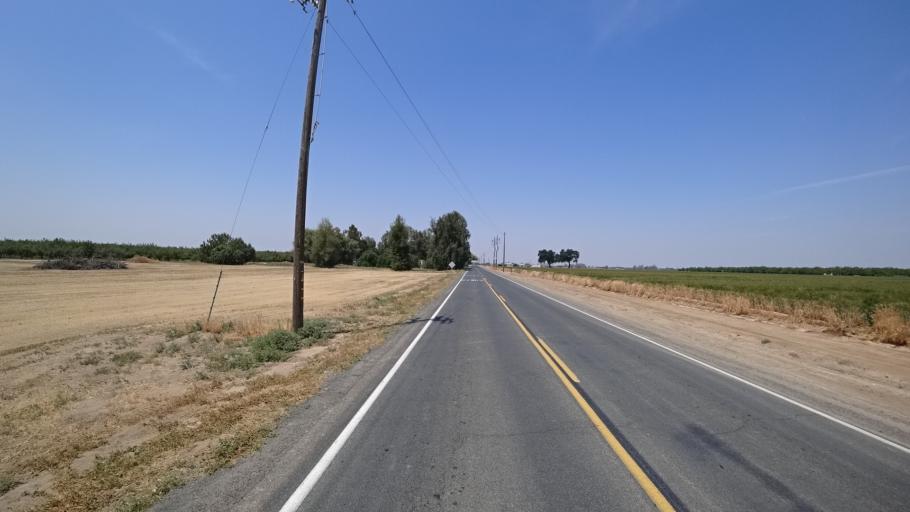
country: US
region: California
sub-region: Kings County
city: Lemoore
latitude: 36.3280
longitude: -119.7820
